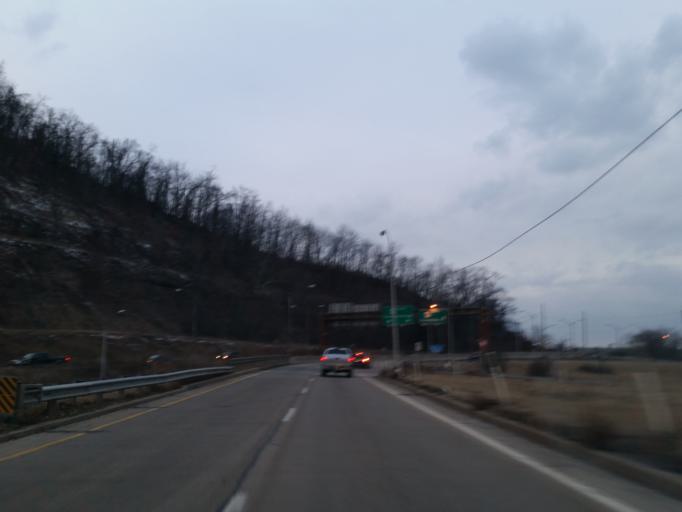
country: US
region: Pennsylvania
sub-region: Allegheny County
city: West Homestead
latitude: 40.3912
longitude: -79.9339
